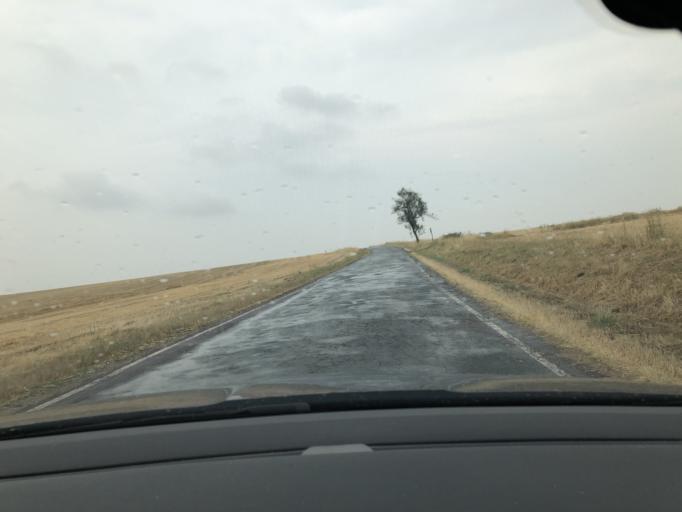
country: CZ
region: South Moravian
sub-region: Okres Znojmo
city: Jevisovice
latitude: 49.0287
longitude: 16.0369
